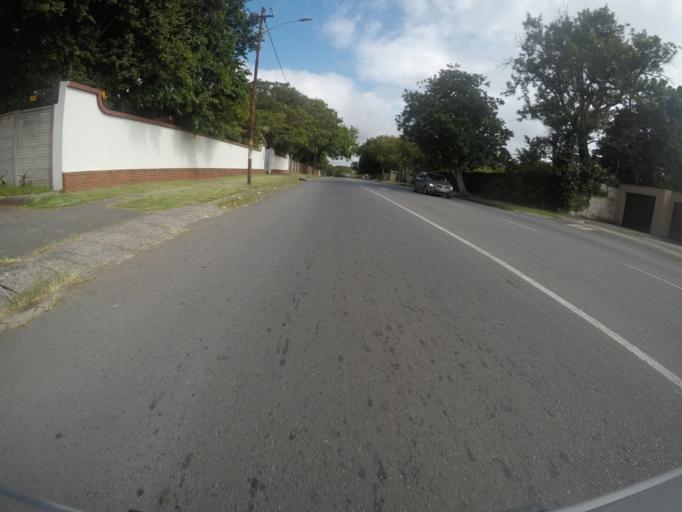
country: ZA
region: Eastern Cape
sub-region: Buffalo City Metropolitan Municipality
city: East London
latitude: -32.9943
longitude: 27.9020
